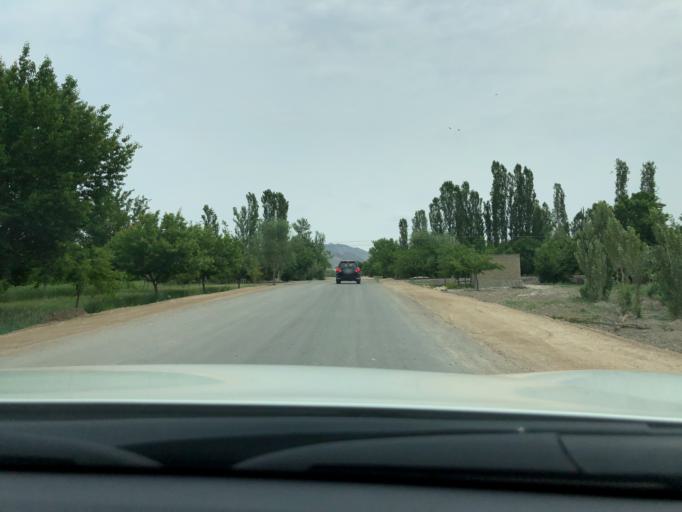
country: TJ
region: Viloyati Sughd
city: Isfara
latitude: 40.1498
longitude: 70.6161
